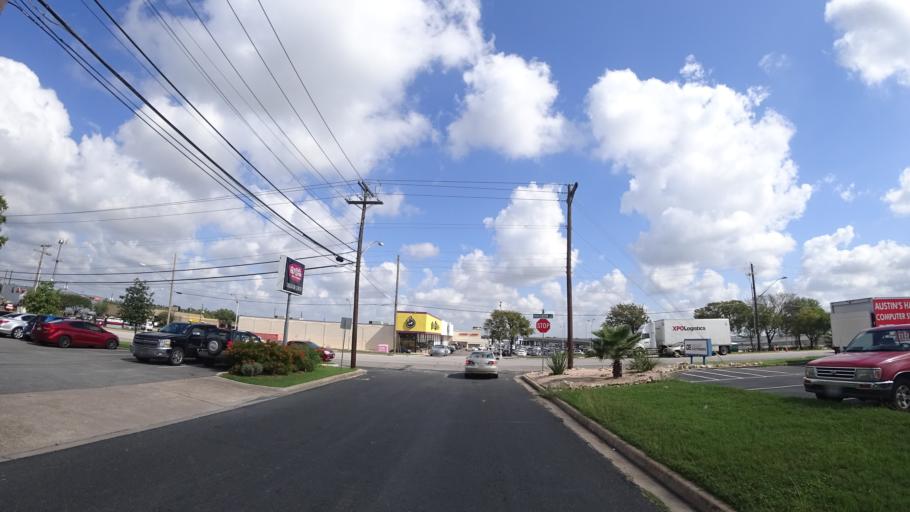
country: US
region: Texas
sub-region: Travis County
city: Austin
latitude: 30.3489
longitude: -97.7164
